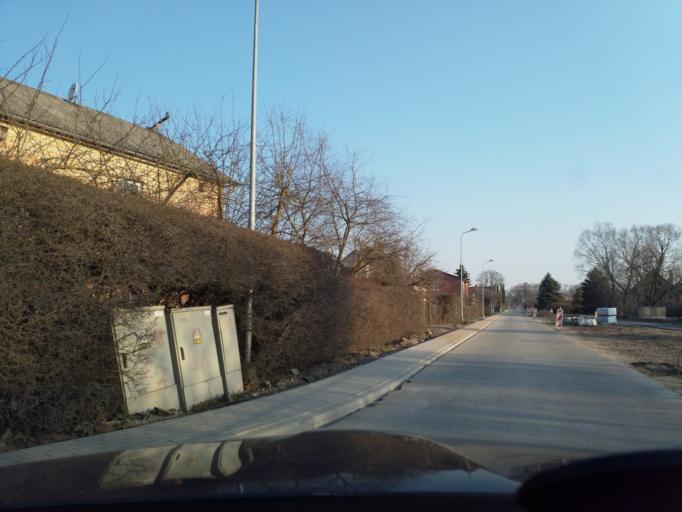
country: LV
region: Grobina
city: Grobina
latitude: 56.5310
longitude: 21.1825
